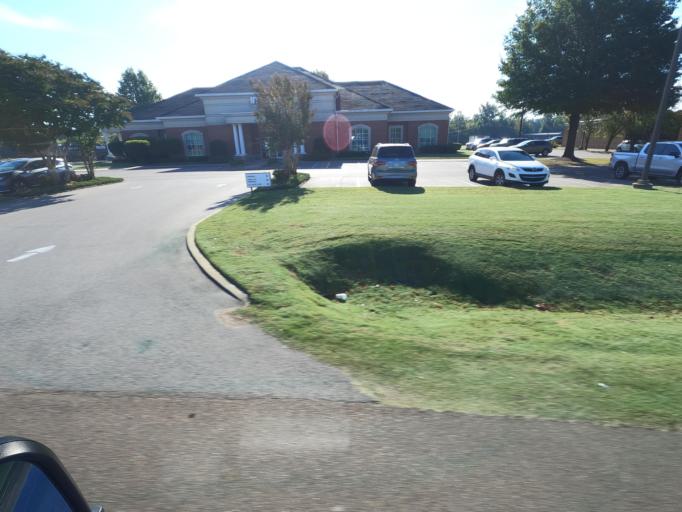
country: US
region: Tennessee
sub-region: Tipton County
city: Atoka
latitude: 35.4488
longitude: -89.7826
